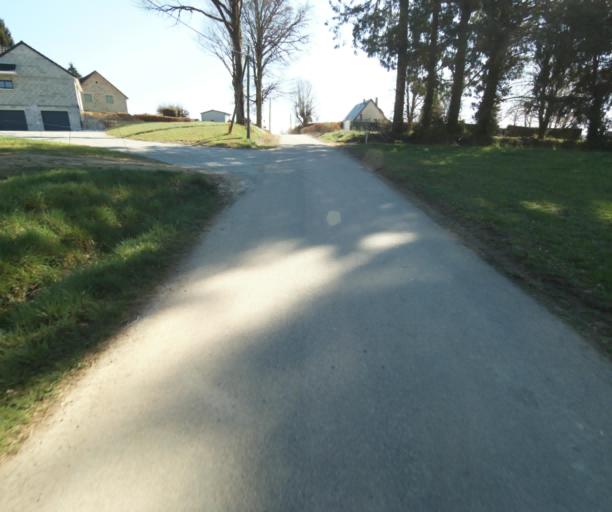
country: FR
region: Limousin
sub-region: Departement de la Correze
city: Chamboulive
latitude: 45.4728
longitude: 1.7359
